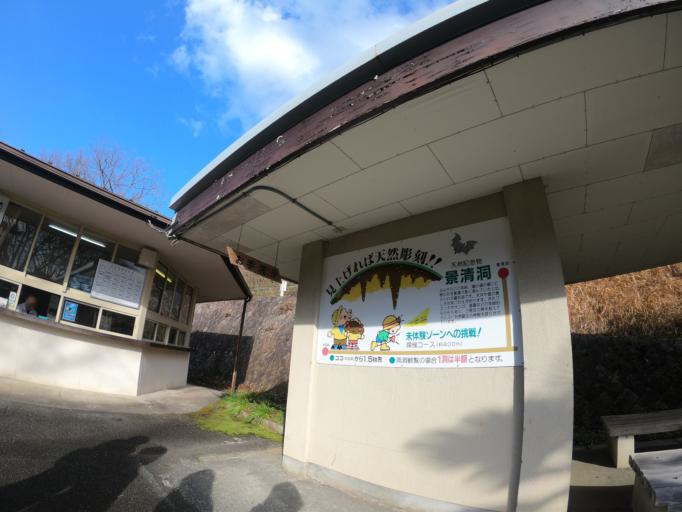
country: JP
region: Yamaguchi
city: Hagi
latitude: 34.2768
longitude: 131.3212
